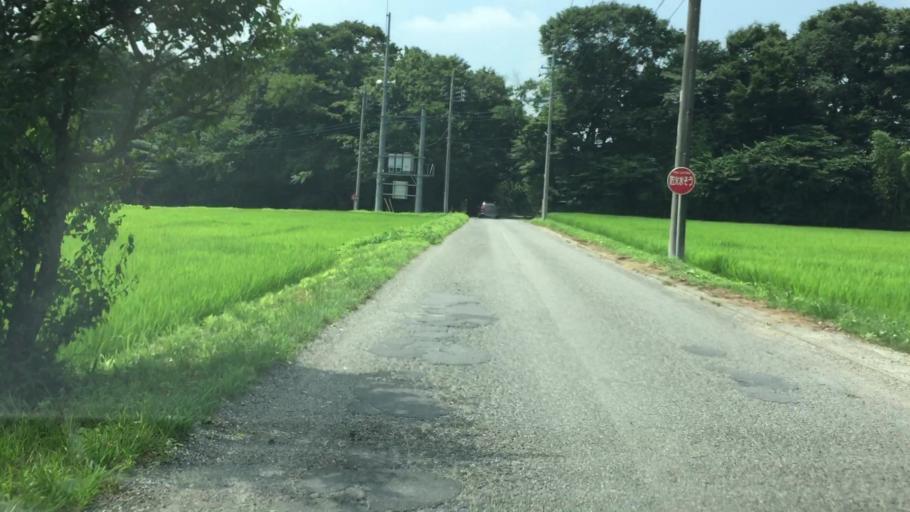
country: JP
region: Tochigi
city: Kuroiso
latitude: 36.9667
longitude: 139.9563
